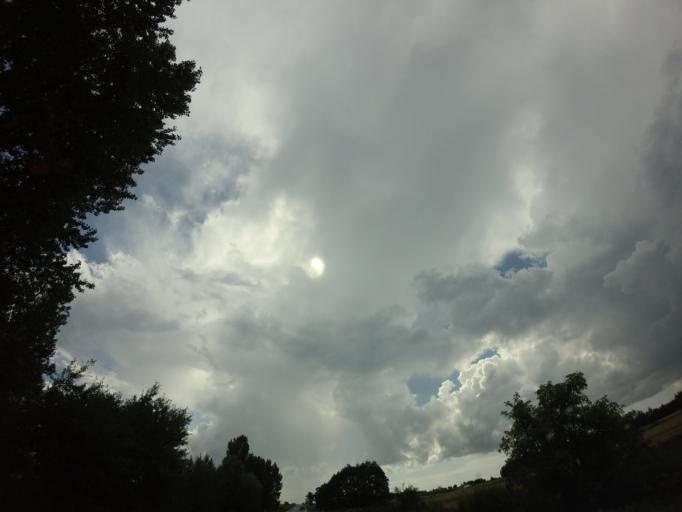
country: PL
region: Swietokrzyskie
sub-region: Powiat buski
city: Stopnica
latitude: 50.4534
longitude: 20.9838
